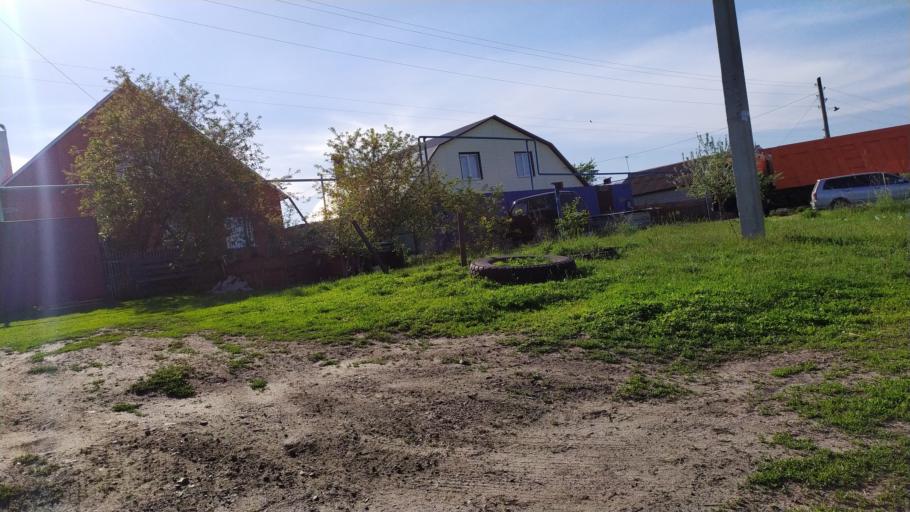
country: RU
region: Kursk
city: Kursk
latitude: 51.6358
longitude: 36.1499
